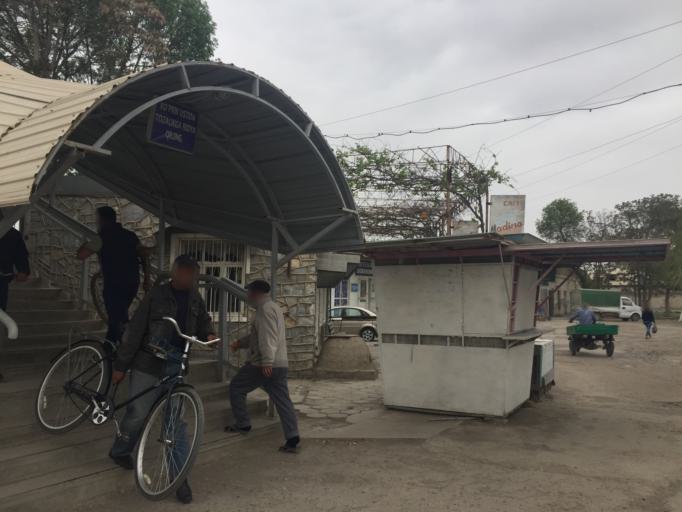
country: UZ
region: Bukhara
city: Kogon
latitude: 39.7205
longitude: 64.5479
